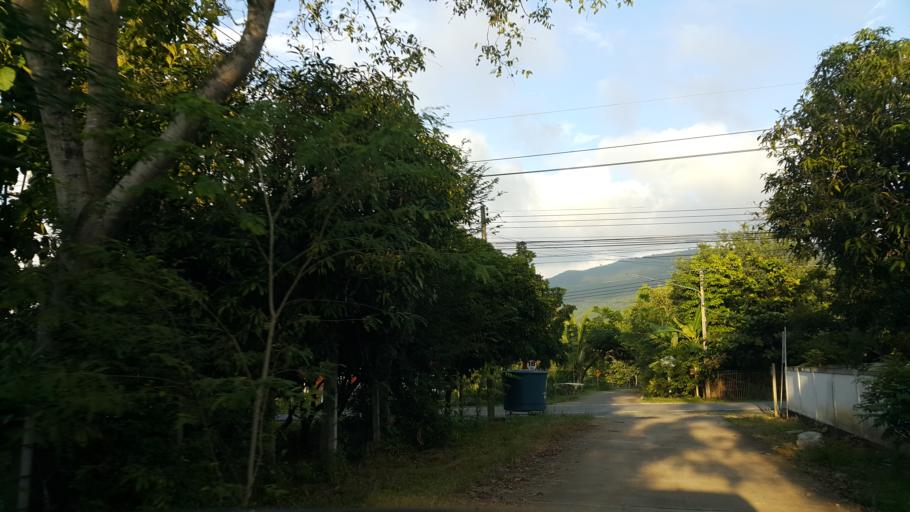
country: TH
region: Chiang Mai
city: Mae On
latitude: 18.7453
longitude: 99.2565
